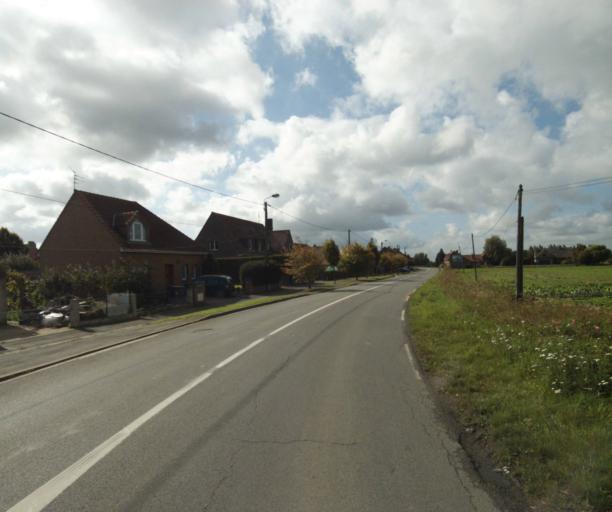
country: FR
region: Nord-Pas-de-Calais
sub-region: Departement du Nord
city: Perenchies
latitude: 50.6801
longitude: 2.9593
